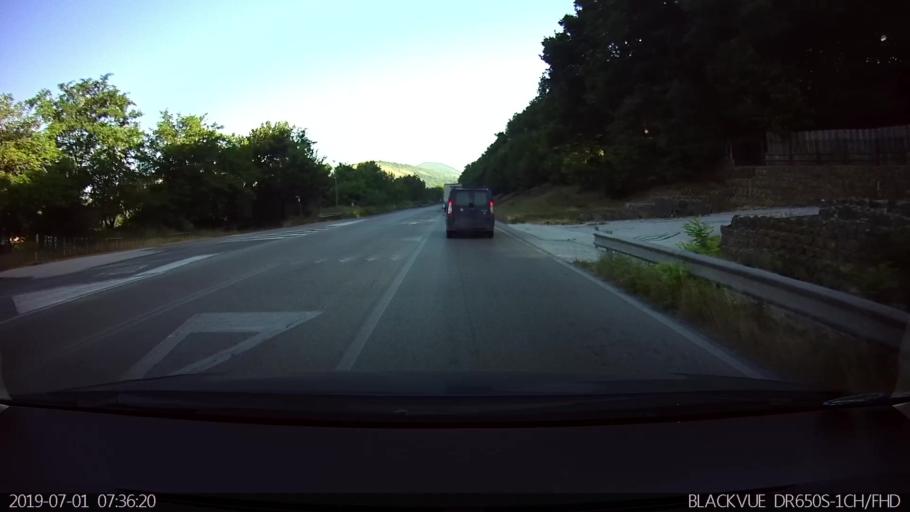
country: IT
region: Latium
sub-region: Provincia di Latina
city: Prossedi
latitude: 41.5307
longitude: 13.2673
